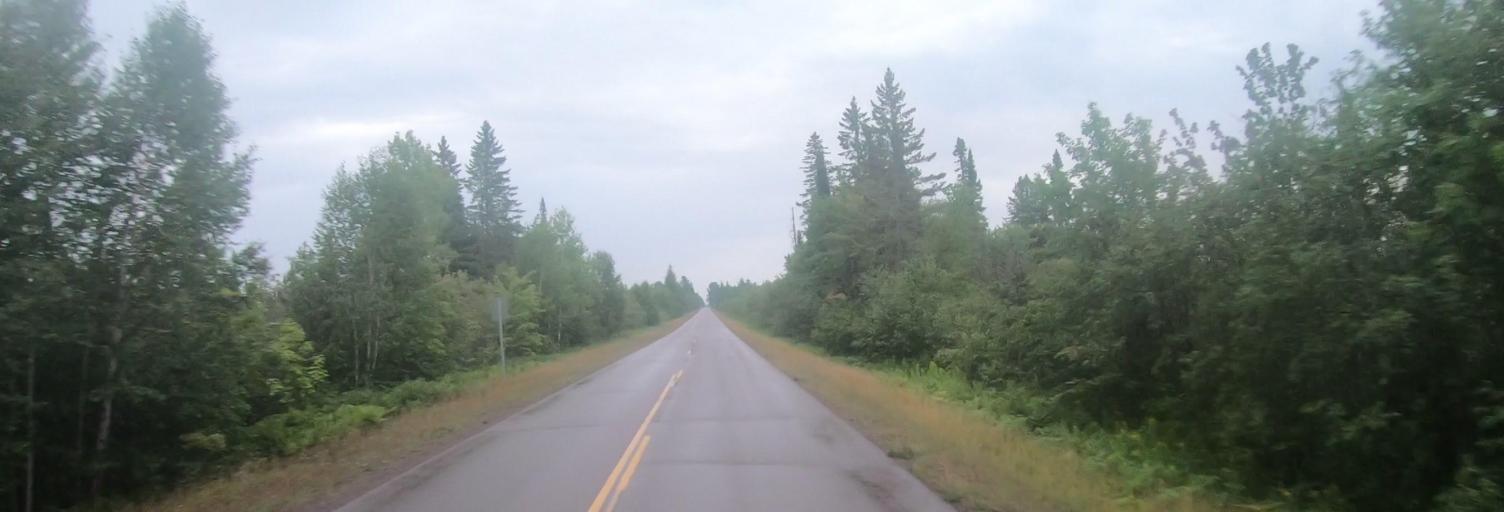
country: US
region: Michigan
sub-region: Keweenaw County
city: Eagle River
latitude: 47.2768
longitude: -88.2654
